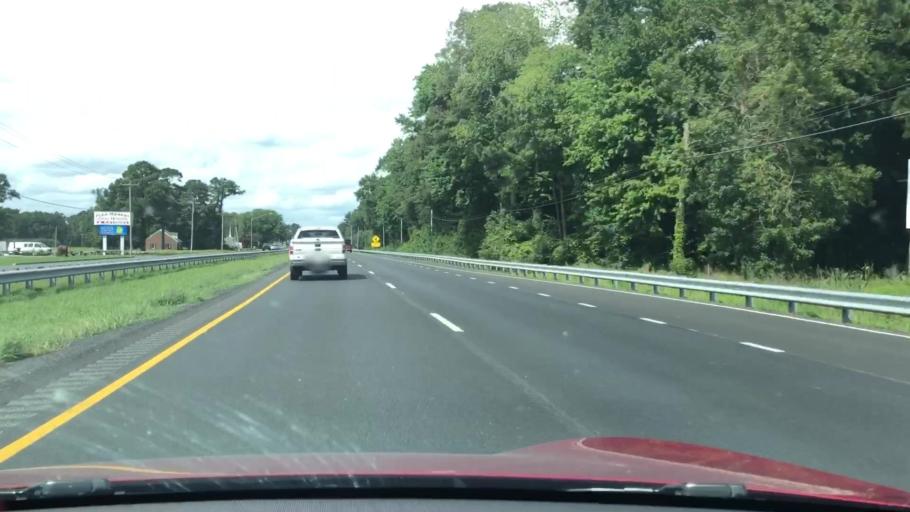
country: US
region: Maryland
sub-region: Worcester County
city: Pocomoke City
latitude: 38.0326
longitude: -75.5410
